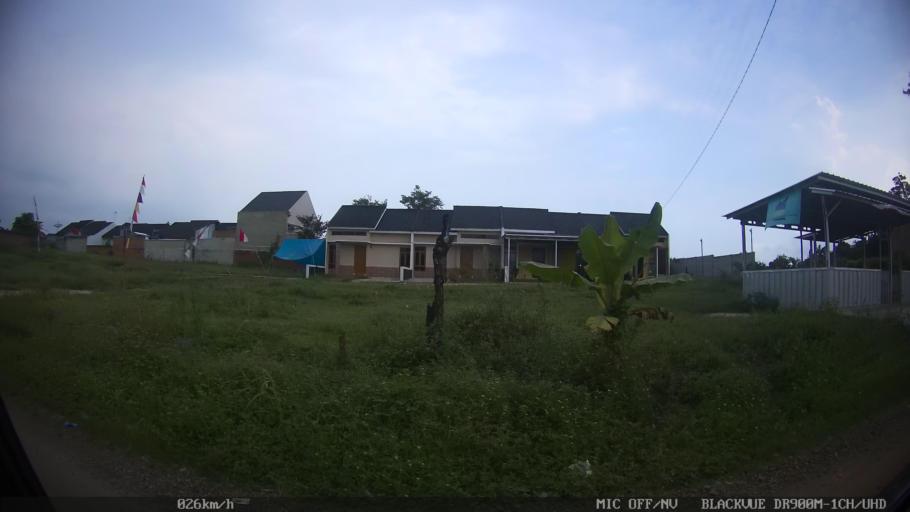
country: ID
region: Lampung
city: Kedaton
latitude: -5.3480
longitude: 105.2329
